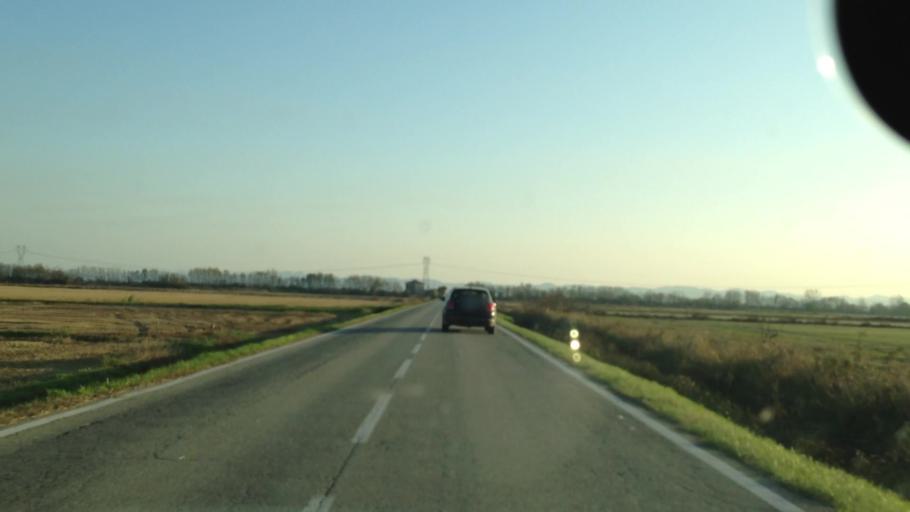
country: IT
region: Piedmont
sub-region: Provincia di Vercelli
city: Lamporo
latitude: 45.2513
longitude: 8.0881
